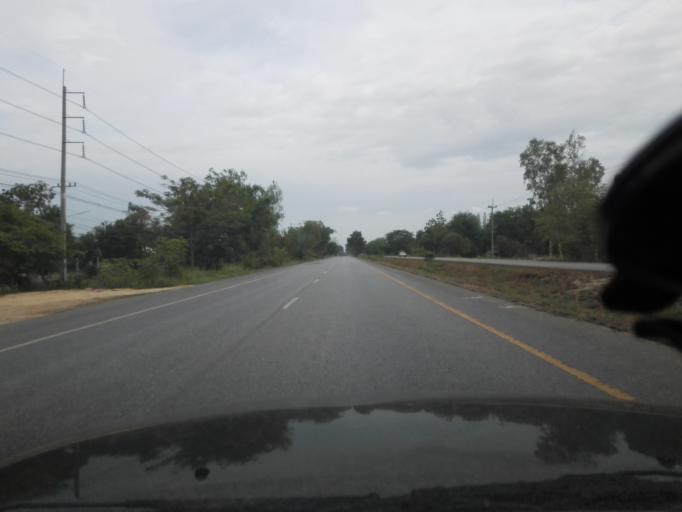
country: TH
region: Kamphaeng Phet
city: Khlong Khlung
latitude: 16.1215
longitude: 99.7196
